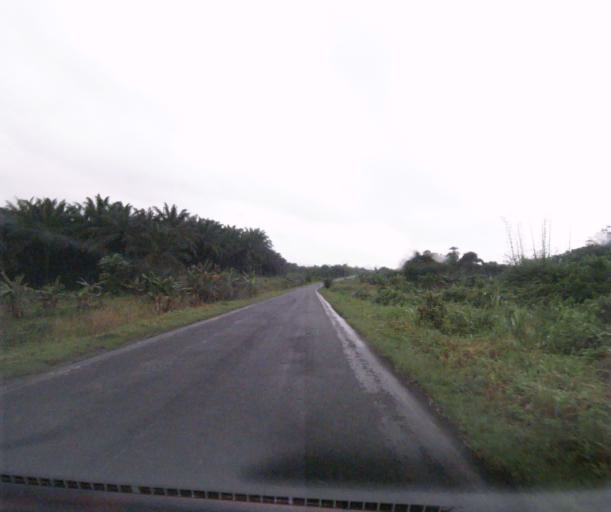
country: CM
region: South-West Province
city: Idenao
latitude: 4.1949
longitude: 9.0030
